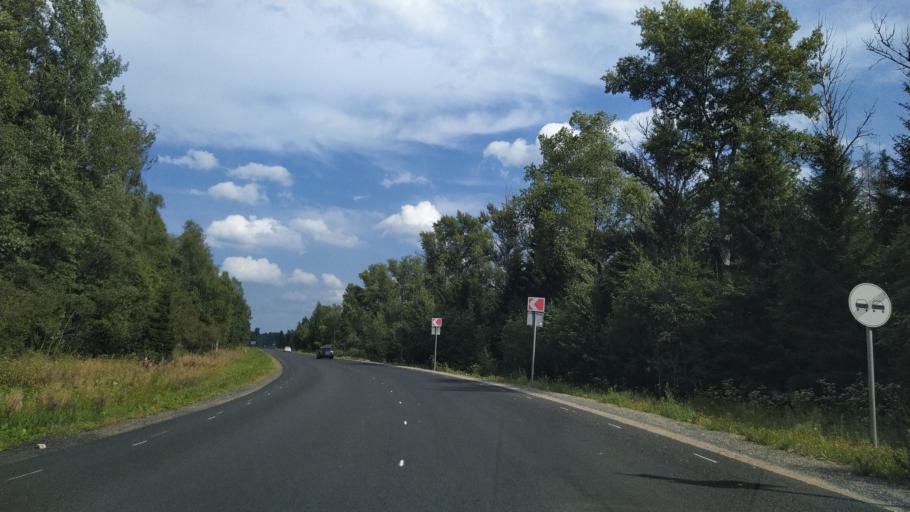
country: RU
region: Pskov
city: Pskov
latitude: 57.7077
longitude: 28.8916
